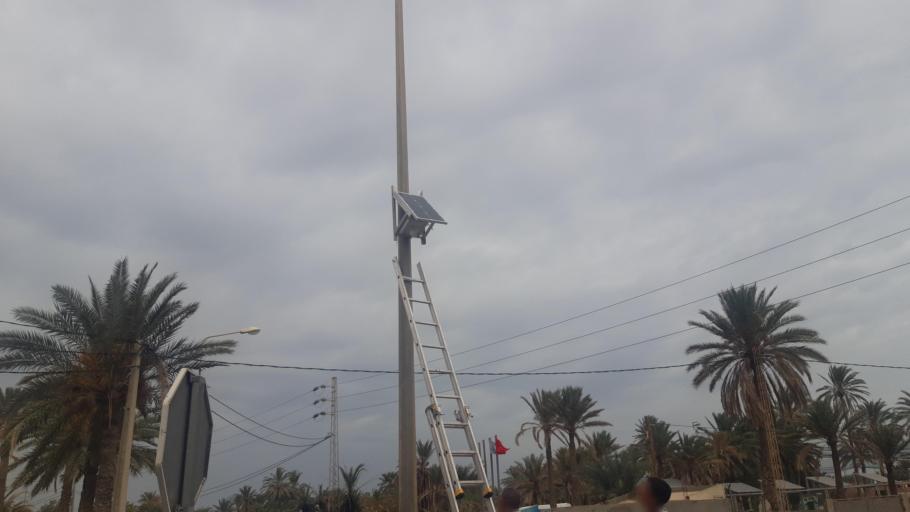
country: TN
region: Qabis
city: Gabes
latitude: 33.8875
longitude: 10.0820
